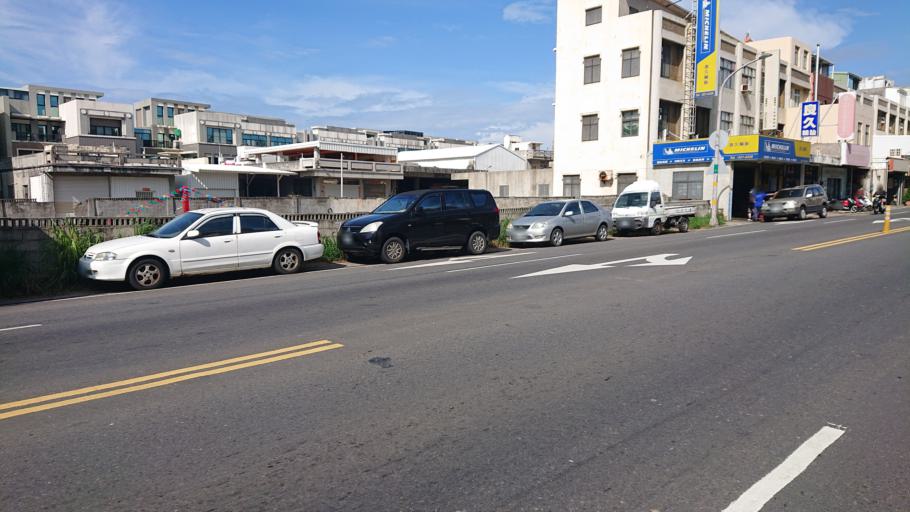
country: TW
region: Taiwan
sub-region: Penghu
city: Ma-kung
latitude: 23.5631
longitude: 119.5907
